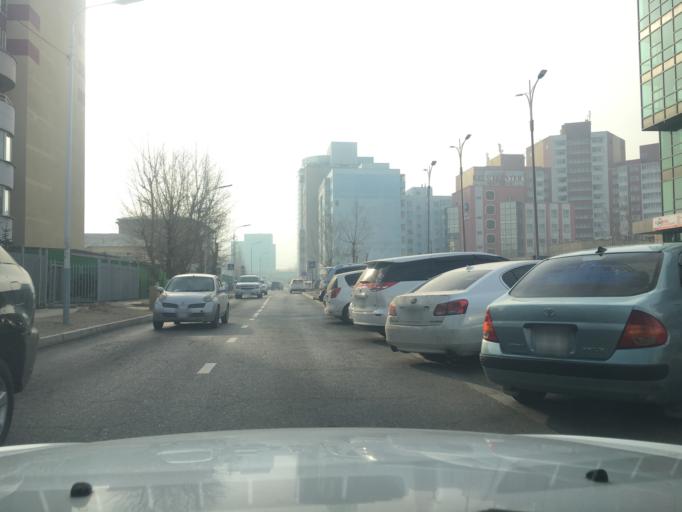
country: MN
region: Ulaanbaatar
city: Ulaanbaatar
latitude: 47.9116
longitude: 106.8774
